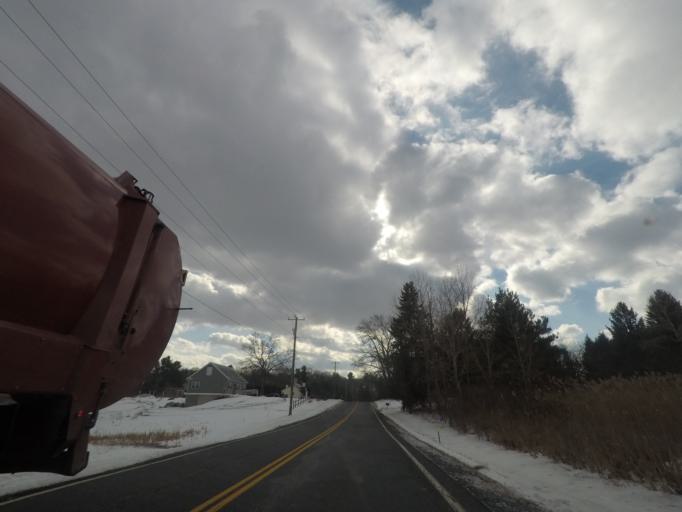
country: US
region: New York
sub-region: Saratoga County
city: Mechanicville
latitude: 42.9015
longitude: -73.7454
